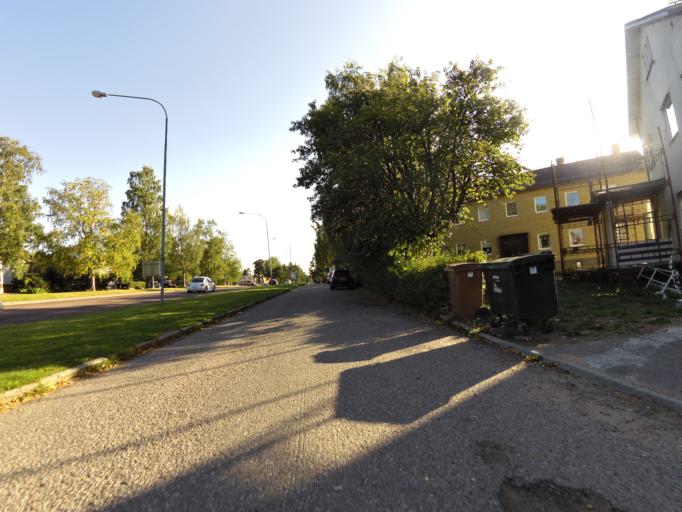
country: SE
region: Gaevleborg
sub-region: Gavle Kommun
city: Gavle
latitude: 60.6639
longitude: 17.1383
